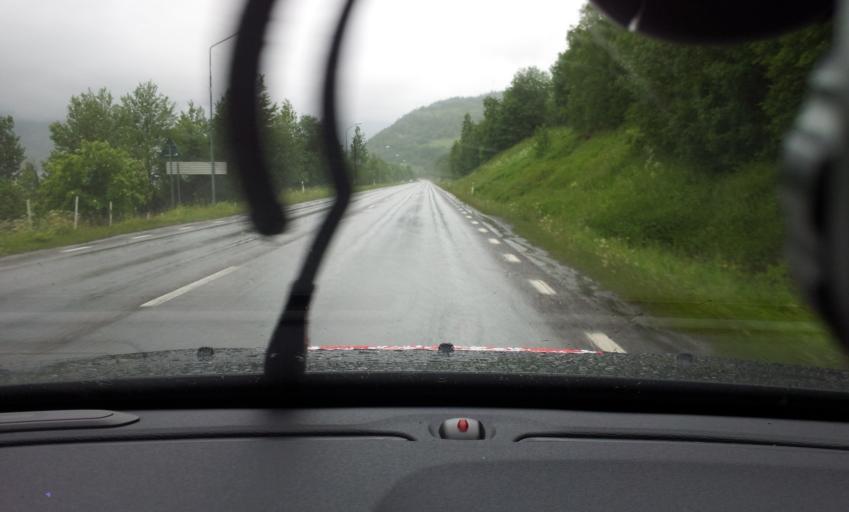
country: SE
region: Jaemtland
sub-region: Are Kommun
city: Are
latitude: 63.3806
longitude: 13.1464
